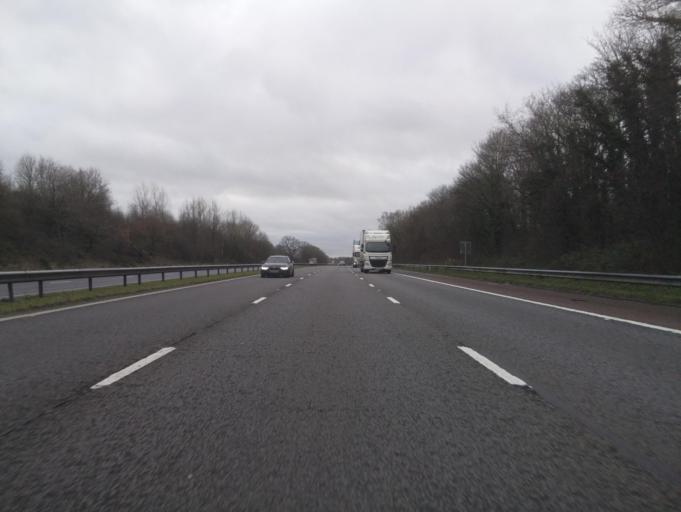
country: GB
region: England
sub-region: Lancashire
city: Garstang
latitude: 53.9324
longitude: -2.7579
